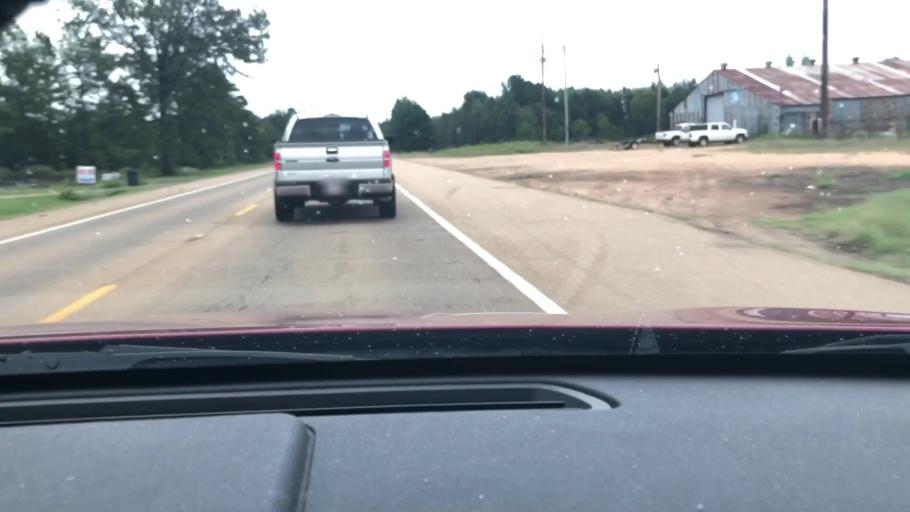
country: US
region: Arkansas
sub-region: Lafayette County
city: Stamps
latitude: 33.3664
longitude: -93.5284
